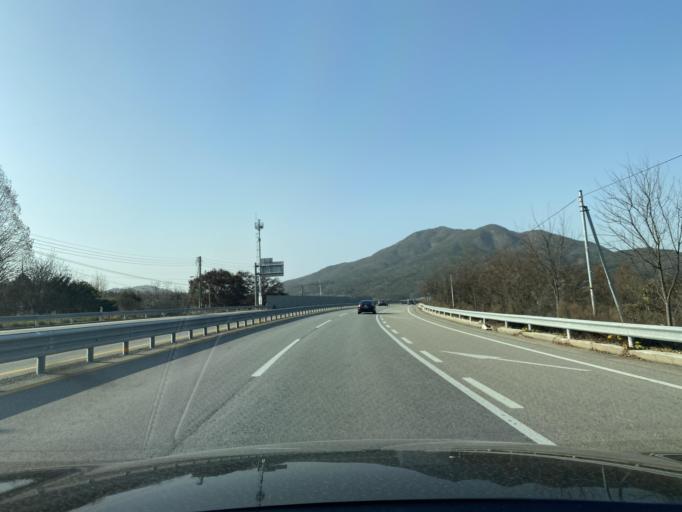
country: KR
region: Chungcheongnam-do
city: Hongsung
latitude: 36.6822
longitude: 126.6572
